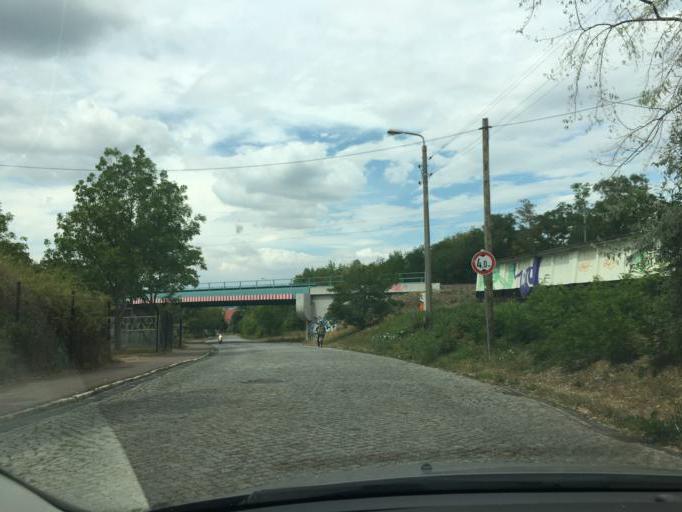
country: DE
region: Saxony-Anhalt
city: Angersdorf
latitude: 51.4489
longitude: 11.9431
